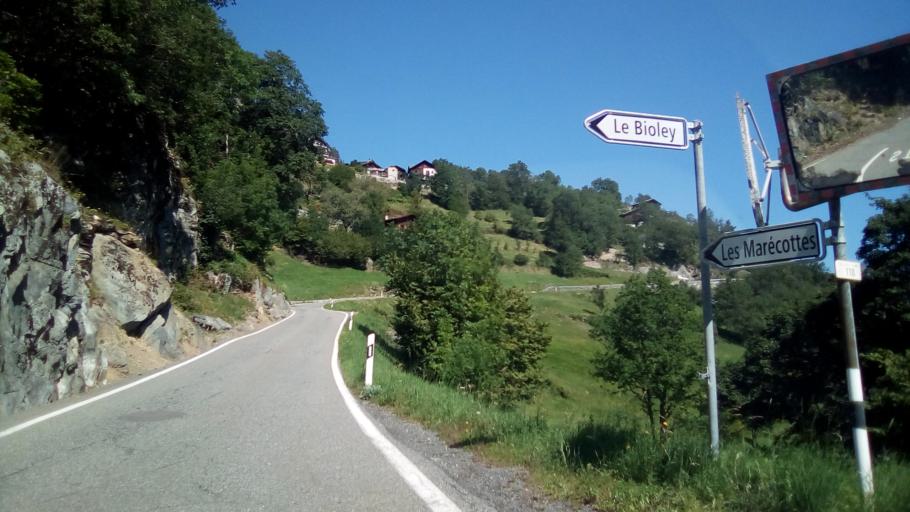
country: CH
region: Valais
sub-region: Saint-Maurice District
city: Salvan
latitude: 46.1255
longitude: 7.0241
